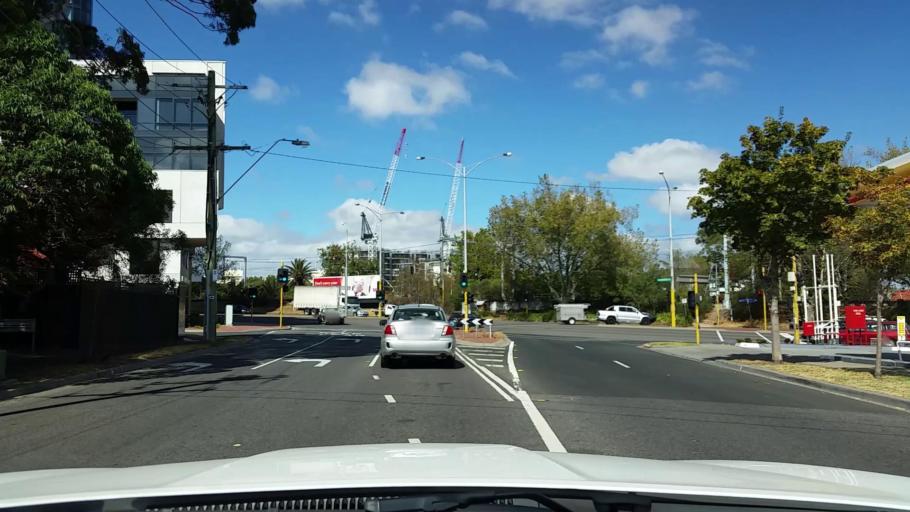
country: AU
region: Victoria
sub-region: Stonnington
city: Malvern East
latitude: -37.8730
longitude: 145.0384
